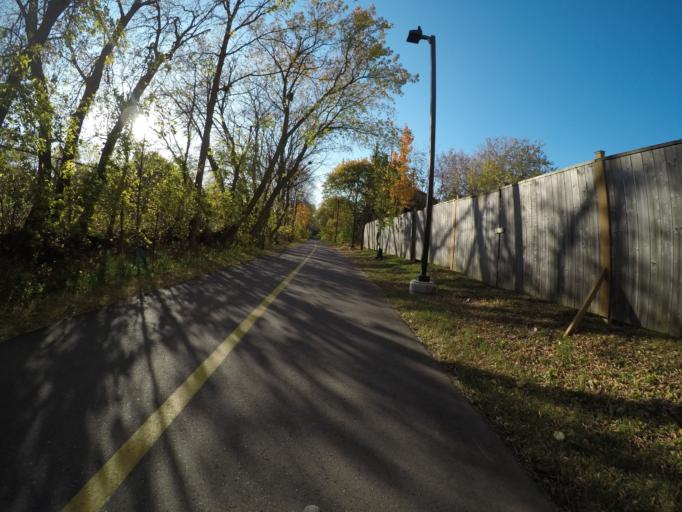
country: CA
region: Ontario
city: Kitchener
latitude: 43.4436
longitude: -80.4964
